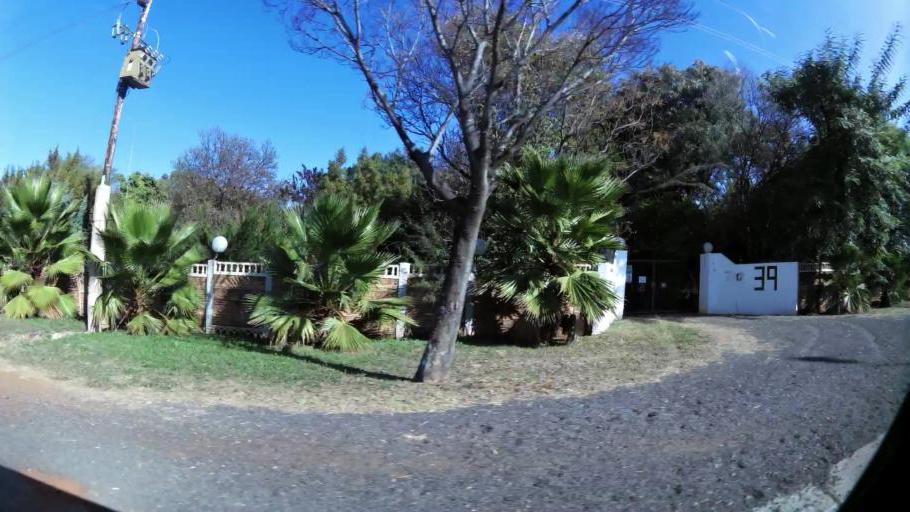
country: ZA
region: Gauteng
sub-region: City of Tshwane Metropolitan Municipality
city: Pretoria
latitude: -25.6645
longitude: 28.1322
